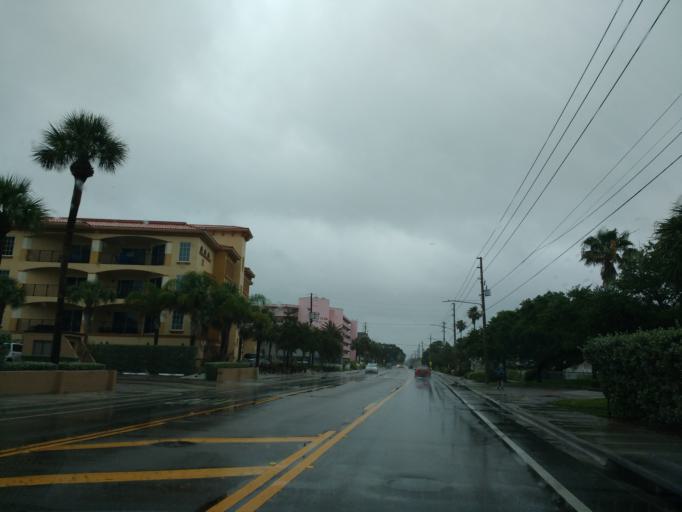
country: US
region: Florida
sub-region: Pinellas County
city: Indian Rocks Beach
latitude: 27.8922
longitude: -82.8493
